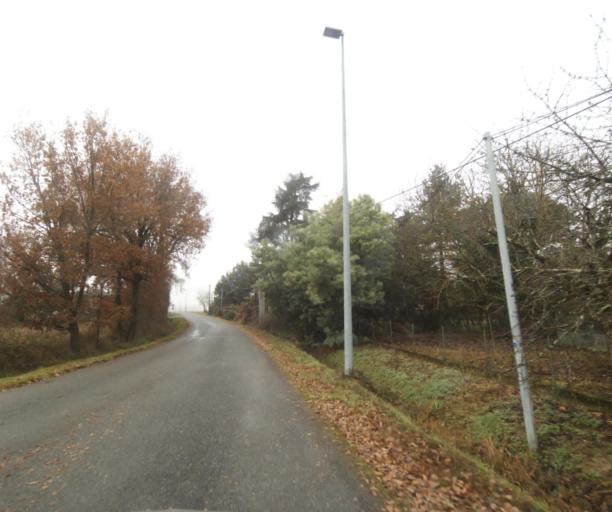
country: FR
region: Midi-Pyrenees
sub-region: Departement du Tarn-et-Garonne
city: Nohic
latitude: 43.8740
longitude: 1.4596
